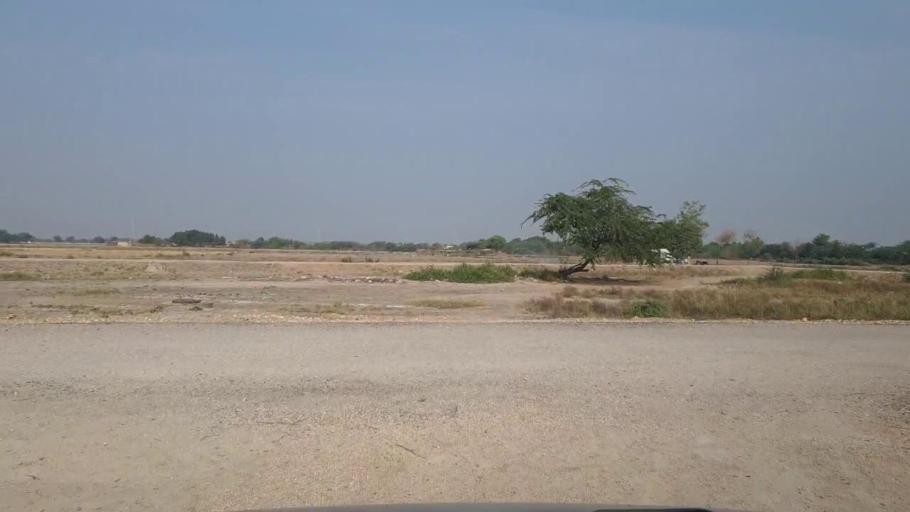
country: PK
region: Sindh
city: Tando Muhammad Khan
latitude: 25.1345
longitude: 68.5210
